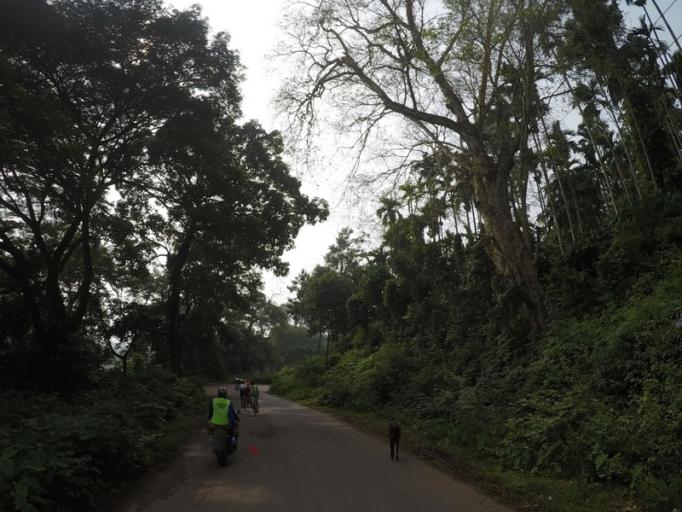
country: IN
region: Karnataka
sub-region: Chikmagalur
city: Koppa
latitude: 13.3455
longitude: 75.4794
